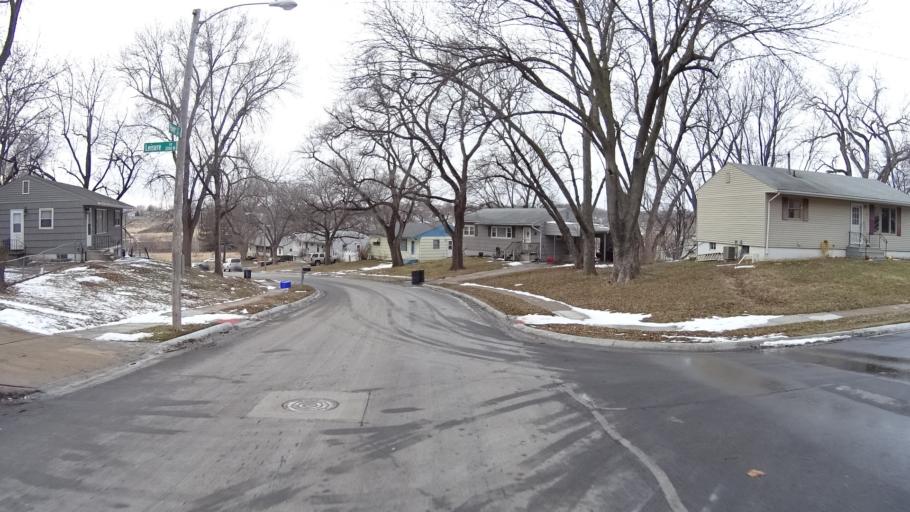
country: US
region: Nebraska
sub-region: Sarpy County
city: Offutt Air Force Base
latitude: 41.1588
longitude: -95.9236
